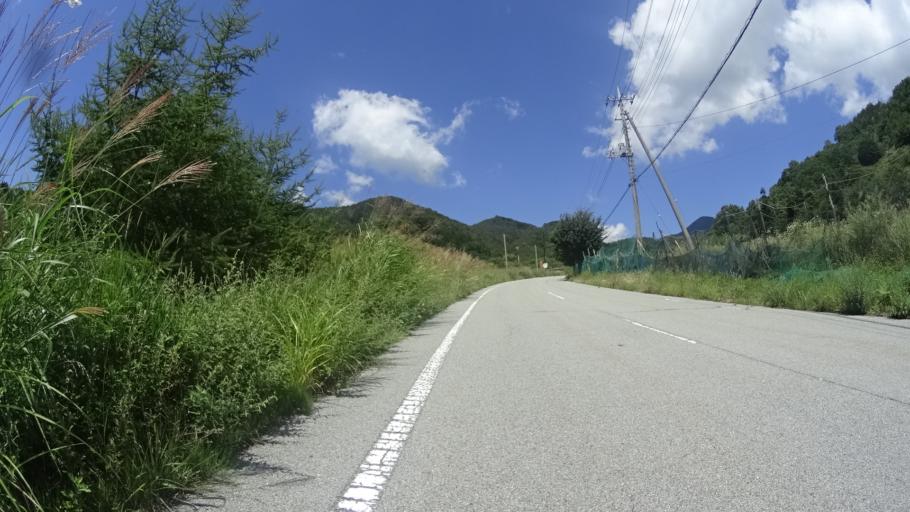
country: JP
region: Yamanashi
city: Enzan
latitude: 35.8088
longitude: 138.6559
